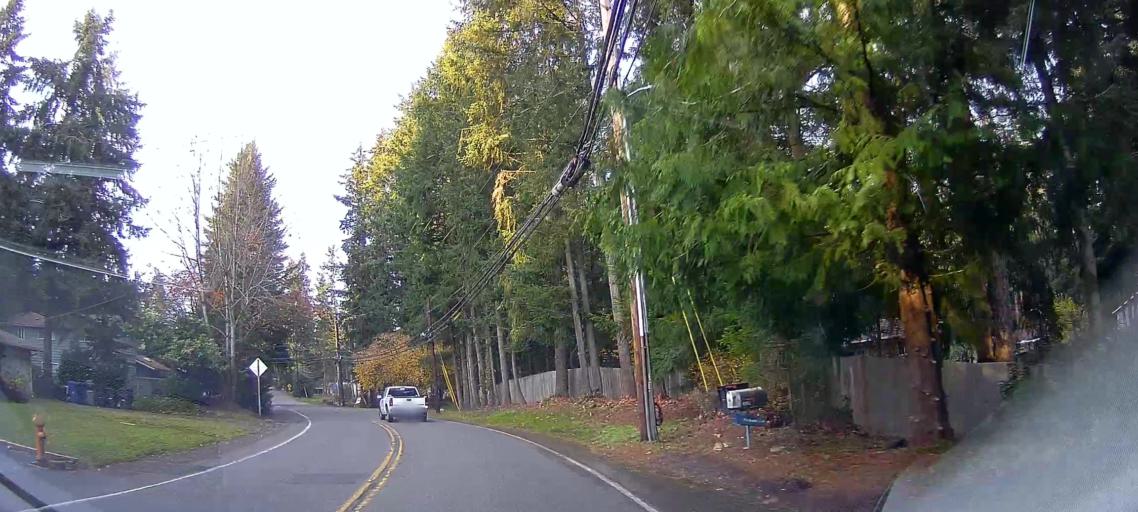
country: US
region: Washington
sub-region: Snohomish County
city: Alderwood Manor
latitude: 47.8161
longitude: -122.2572
